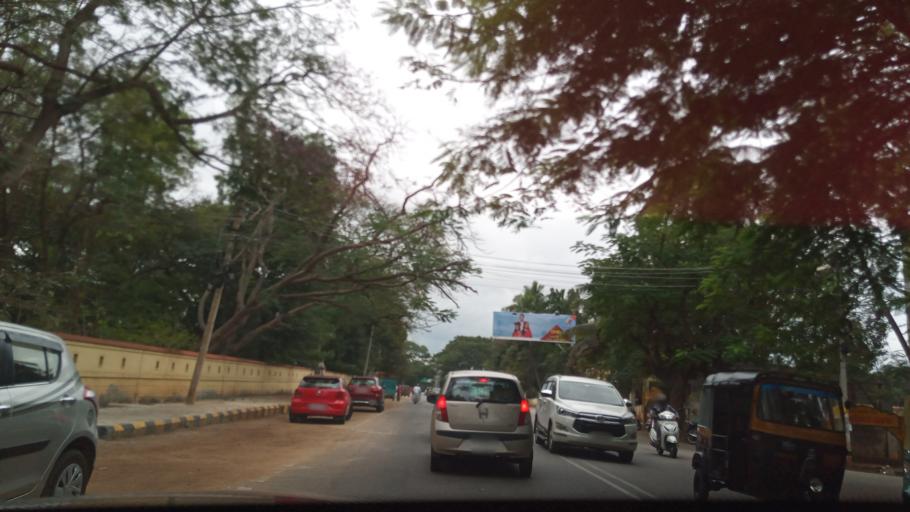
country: IN
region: Karnataka
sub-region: Mysore
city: Mysore
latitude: 12.3049
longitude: 76.6355
